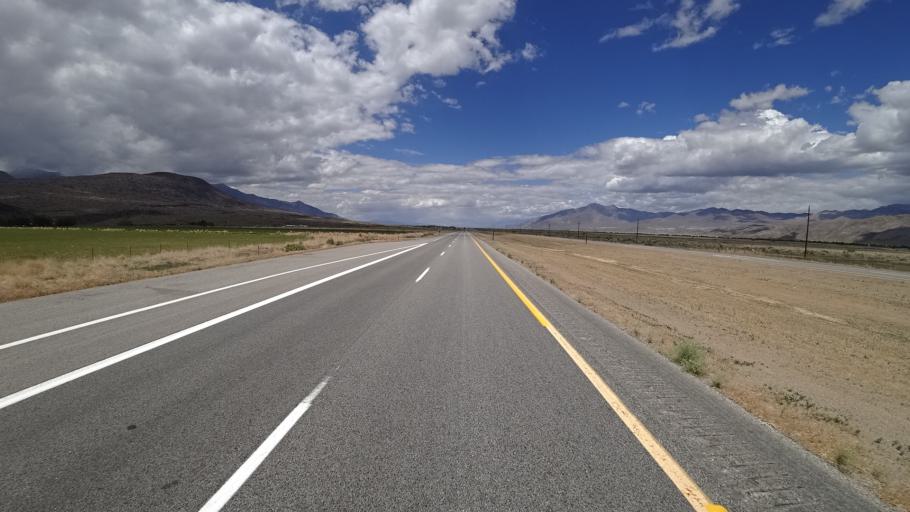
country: US
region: California
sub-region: Inyo County
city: Big Pine
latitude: 37.0862
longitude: -118.2469
